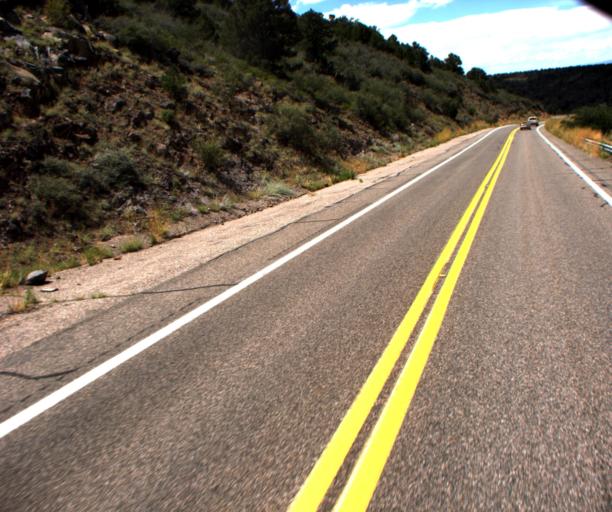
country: US
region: Arizona
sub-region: Yavapai County
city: Lake Montezuma
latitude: 34.5025
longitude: -111.6420
